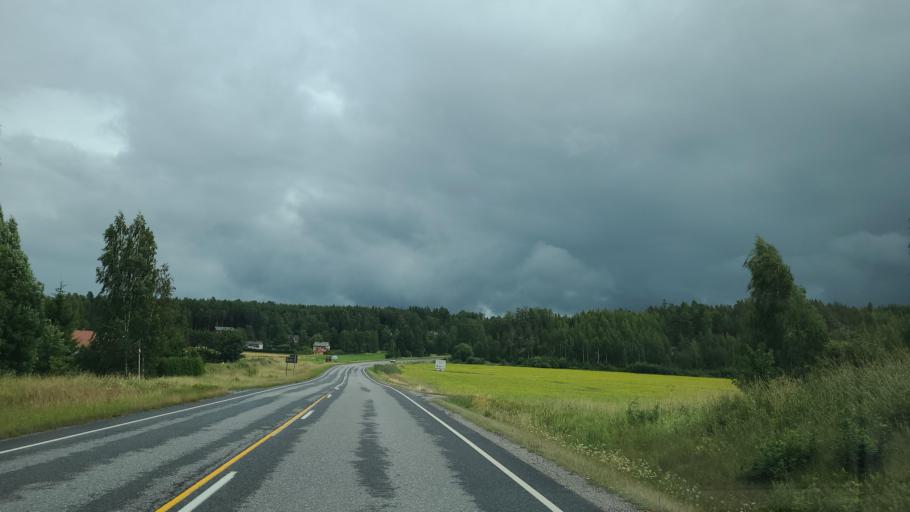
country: FI
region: Varsinais-Suomi
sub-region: Turku
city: Sauvo
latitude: 60.3407
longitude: 22.6931
